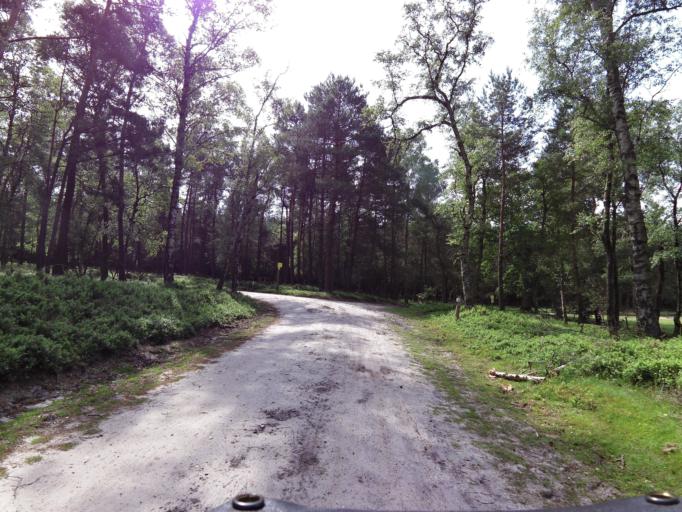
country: NL
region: Gelderland
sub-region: Gemeente Apeldoorn
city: Loenen
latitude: 52.0793
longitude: 5.9833
